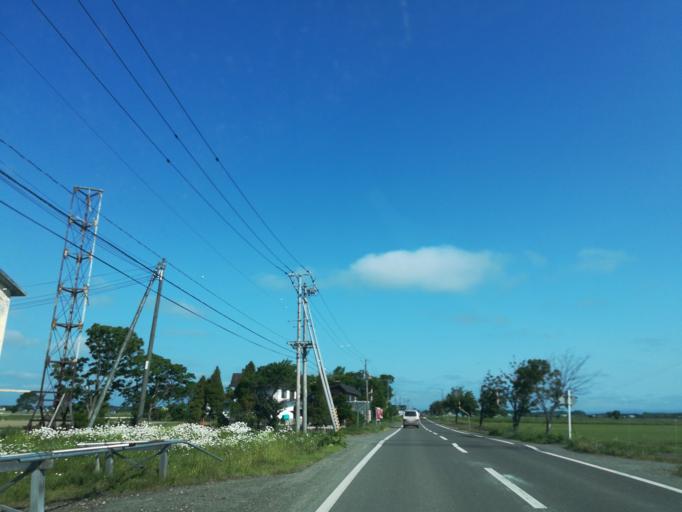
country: JP
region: Hokkaido
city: Iwamizawa
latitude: 43.1675
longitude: 141.7339
